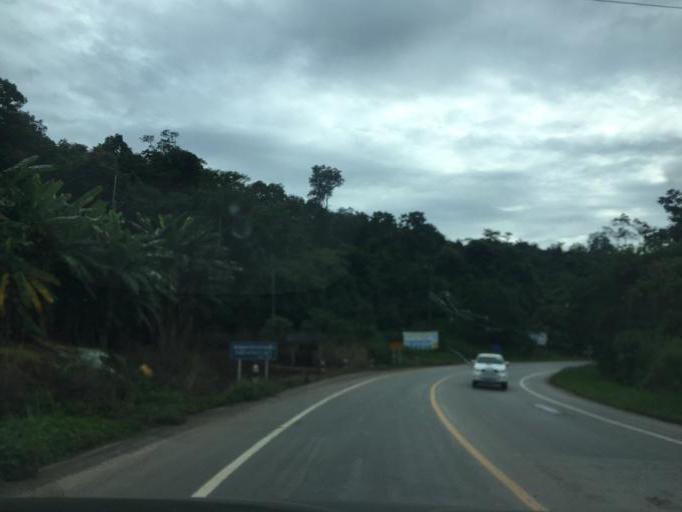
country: TH
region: Lampang
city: Wang Nuea
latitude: 19.1079
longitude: 99.4522
